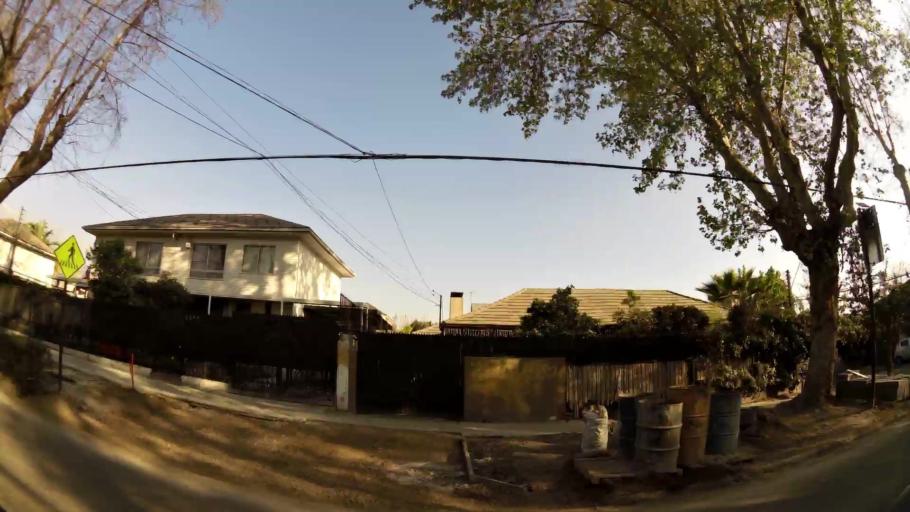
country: CL
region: Santiago Metropolitan
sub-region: Provincia de Santiago
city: Villa Presidente Frei, Nunoa, Santiago, Chile
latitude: -33.4477
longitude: -70.5685
